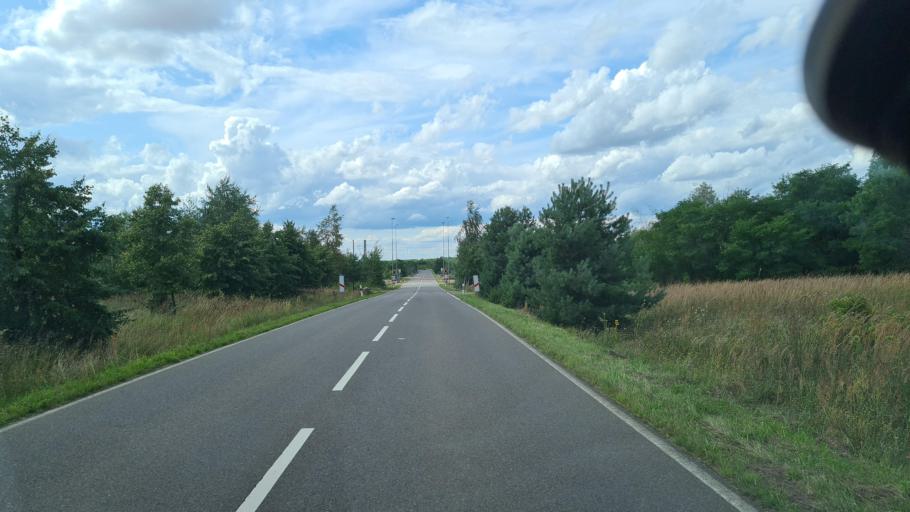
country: DE
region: Brandenburg
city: Spremberg
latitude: 51.5917
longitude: 14.3111
